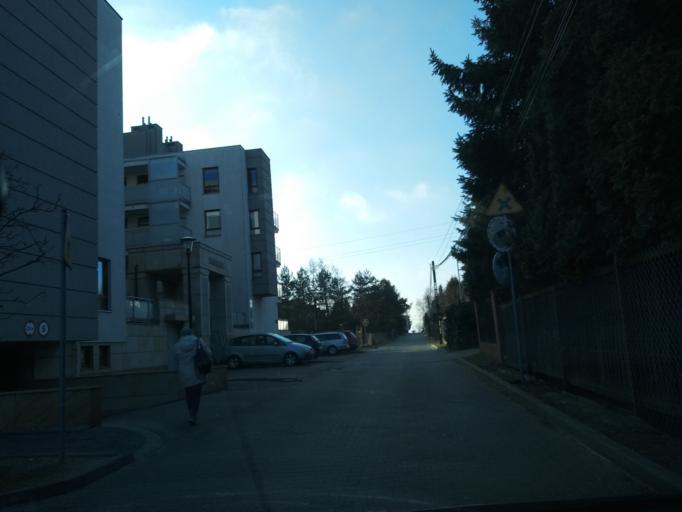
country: PL
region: Masovian Voivodeship
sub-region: Powiat piaseczynski
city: Mysiadlo
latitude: 52.0938
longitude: 21.0121
